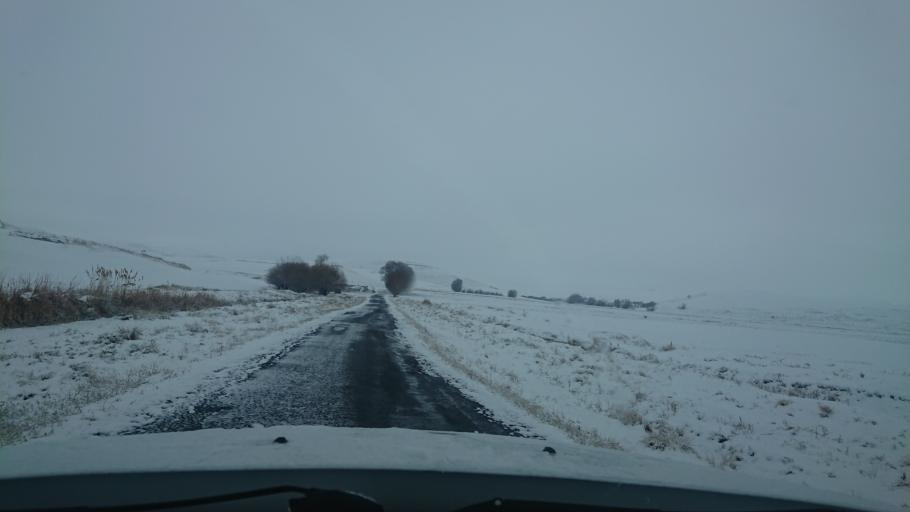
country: TR
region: Aksaray
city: Acipinar
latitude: 38.6835
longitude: 33.8654
